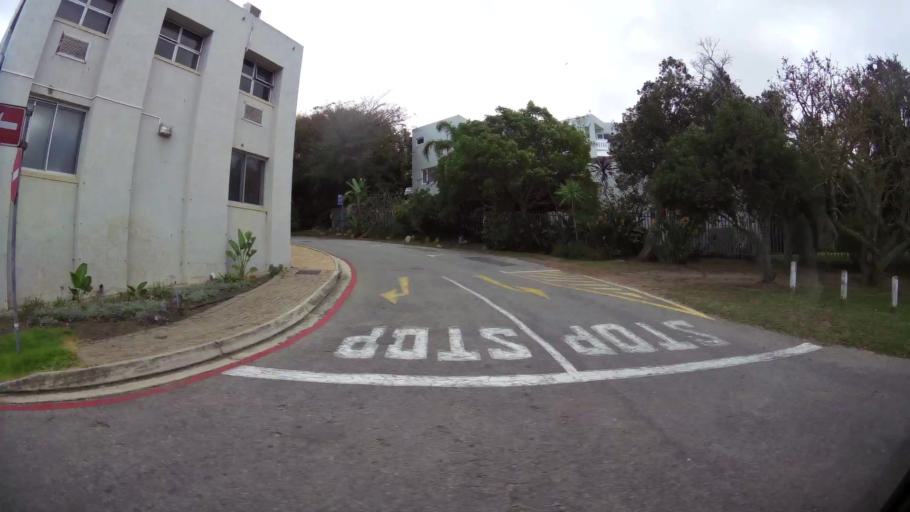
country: ZA
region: Western Cape
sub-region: Eden District Municipality
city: Plettenberg Bay
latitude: -34.0543
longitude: 23.3734
